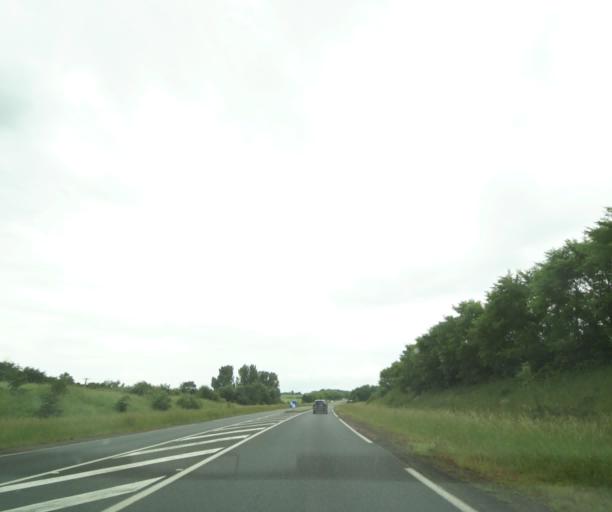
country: FR
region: Poitou-Charentes
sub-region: Departement des Deux-Sevres
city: Airvault
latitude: 46.8090
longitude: -0.2112
